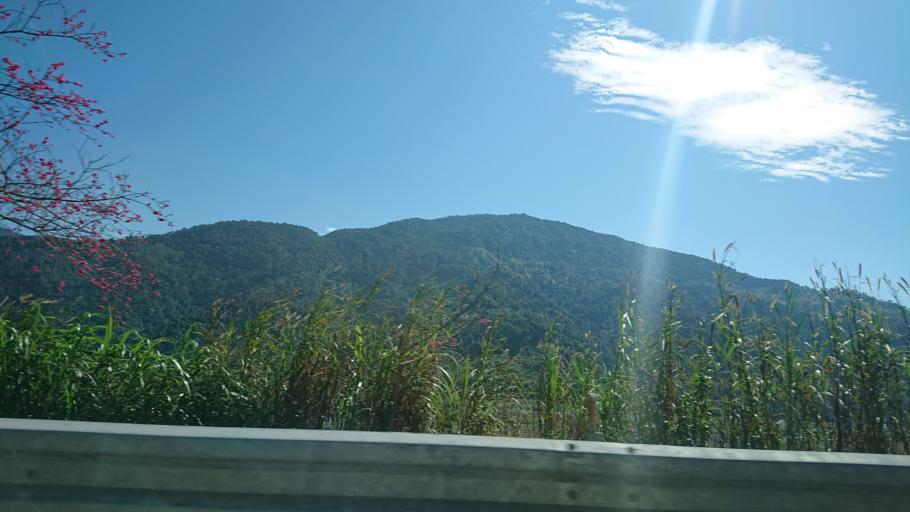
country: TW
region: Taiwan
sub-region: Yilan
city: Yilan
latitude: 24.5952
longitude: 121.5105
